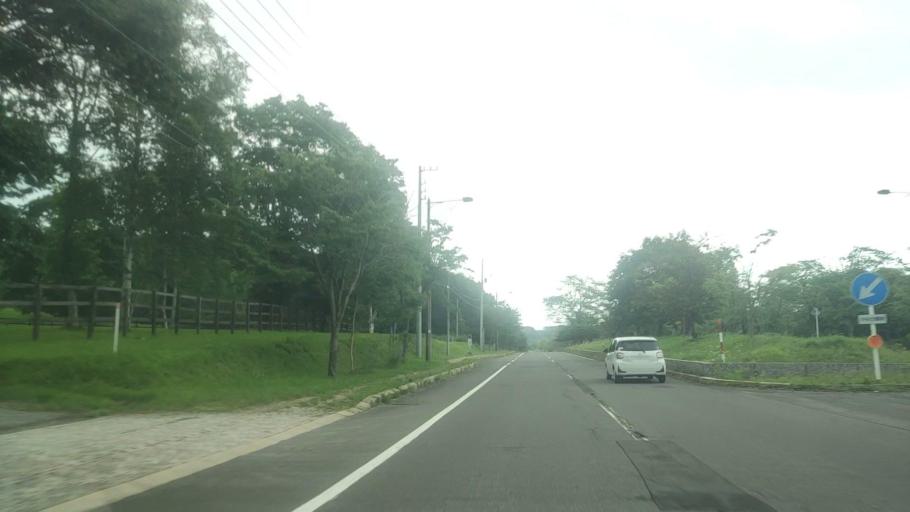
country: JP
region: Hokkaido
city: Shiraoi
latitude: 42.4690
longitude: 141.1609
